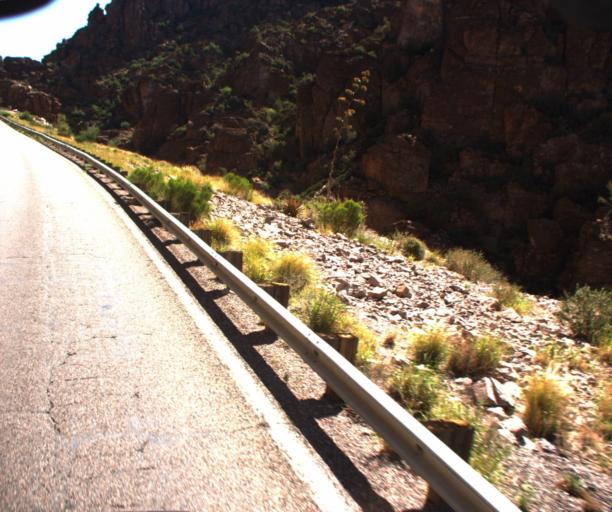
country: US
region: Arizona
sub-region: Pinal County
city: Superior
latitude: 33.3065
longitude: -111.0756
